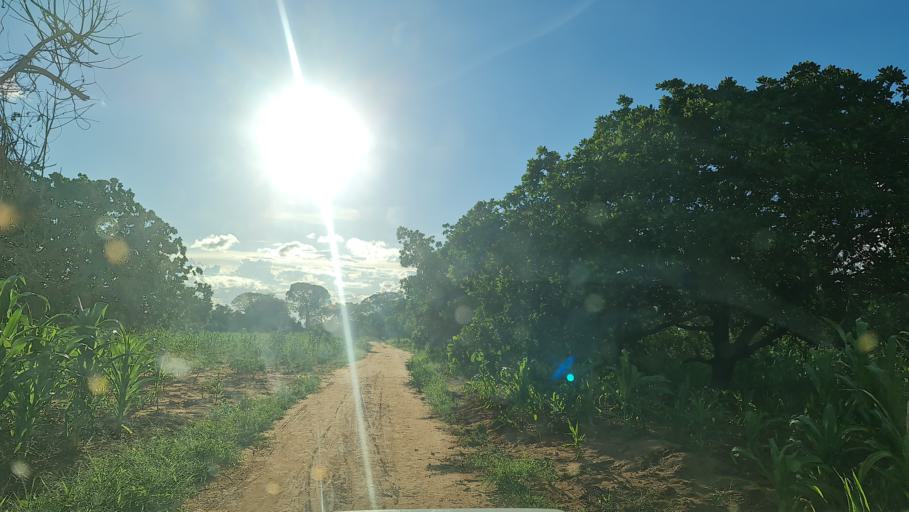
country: MZ
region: Nampula
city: Ilha de Mocambique
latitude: -14.9439
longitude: 40.1601
